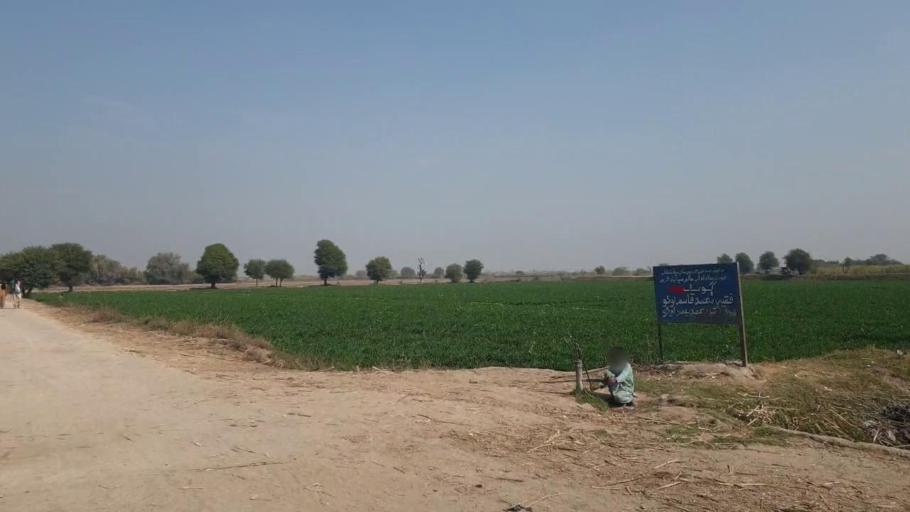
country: PK
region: Sindh
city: Chambar
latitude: 25.3442
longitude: 68.8518
